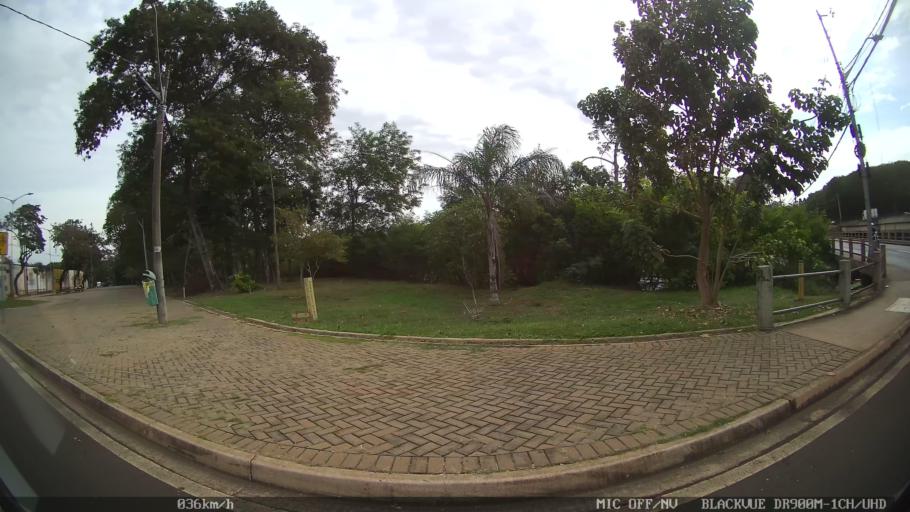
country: BR
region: Sao Paulo
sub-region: Piracicaba
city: Piracicaba
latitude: -22.7063
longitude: -47.6472
